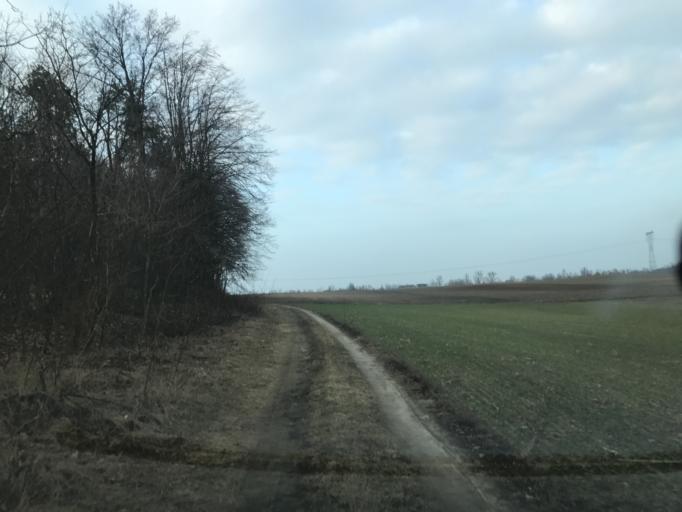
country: PL
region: Kujawsko-Pomorskie
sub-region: Powiat golubsko-dobrzynski
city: Golub-Dobrzyn
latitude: 53.1781
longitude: 18.9996
